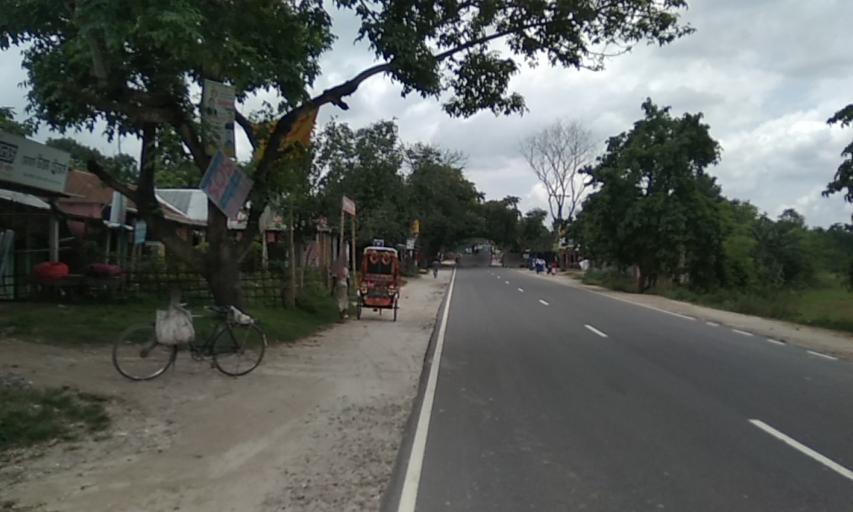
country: BD
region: Rangpur Division
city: Rangpur
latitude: 25.8003
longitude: 89.1900
